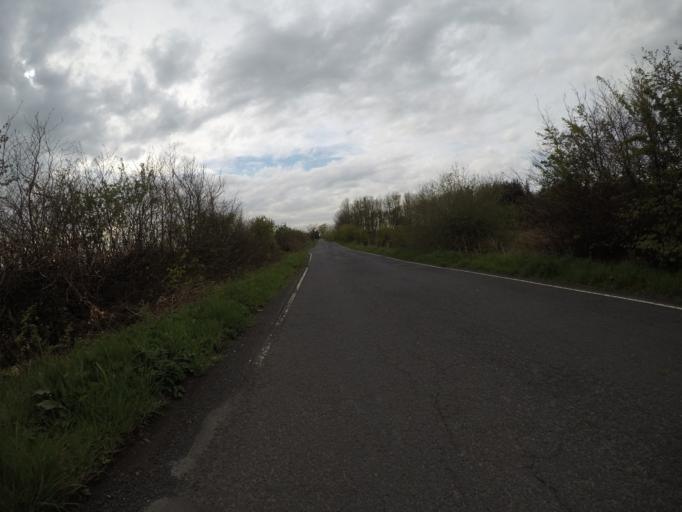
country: GB
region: Scotland
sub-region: East Ayrshire
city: Kilmarnock
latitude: 55.6437
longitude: -4.4812
